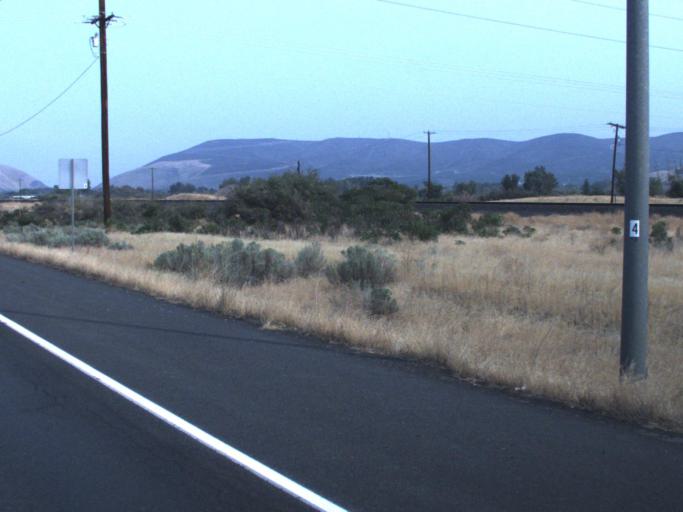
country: US
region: Washington
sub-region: Yakima County
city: Wapato
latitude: 46.4918
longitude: -120.4579
